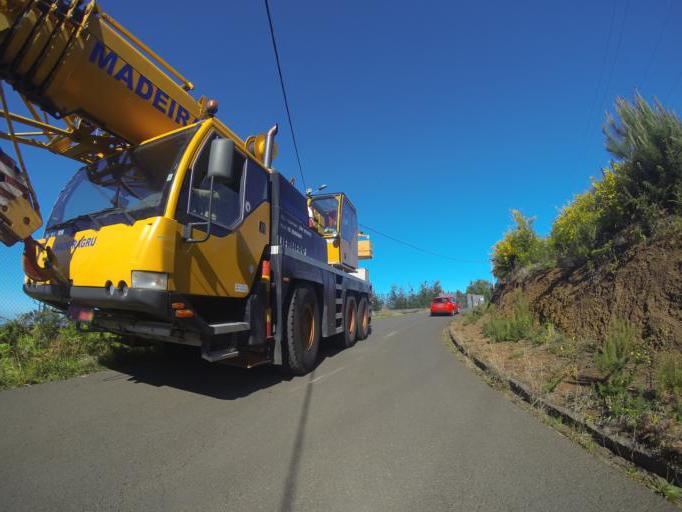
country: PT
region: Madeira
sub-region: Calheta
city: Estreito da Calheta
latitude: 32.7614
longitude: -17.1979
